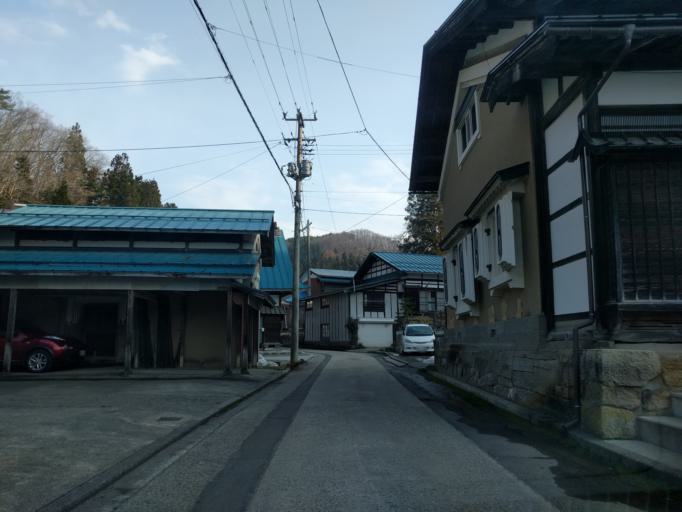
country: JP
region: Fukushima
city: Kitakata
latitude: 37.7059
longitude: 139.9114
